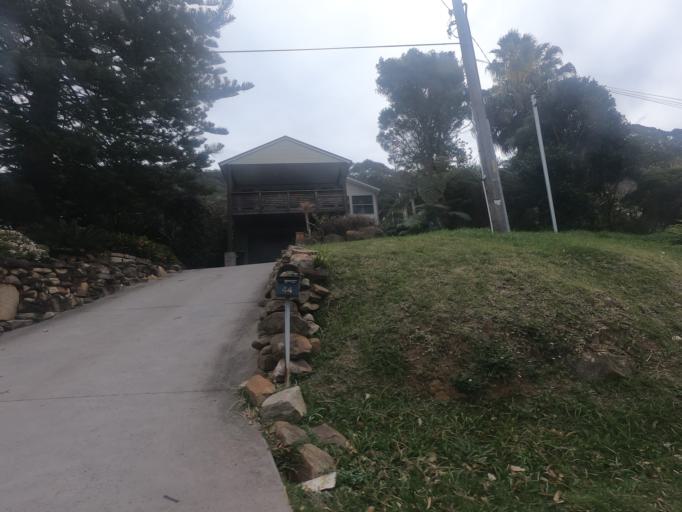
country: AU
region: New South Wales
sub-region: Wollongong
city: Bulli
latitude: -34.2914
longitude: 150.9369
